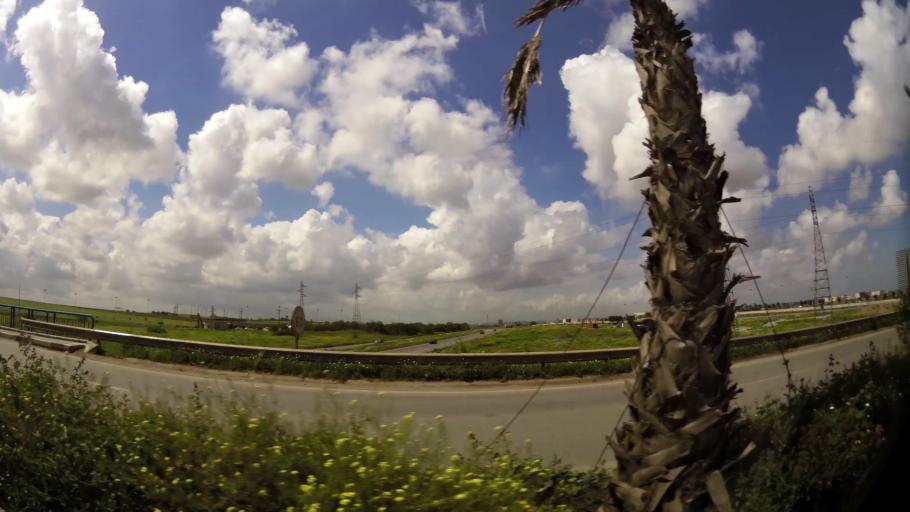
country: MA
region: Grand Casablanca
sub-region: Mediouna
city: Tit Mellil
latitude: 33.5636
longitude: -7.4967
